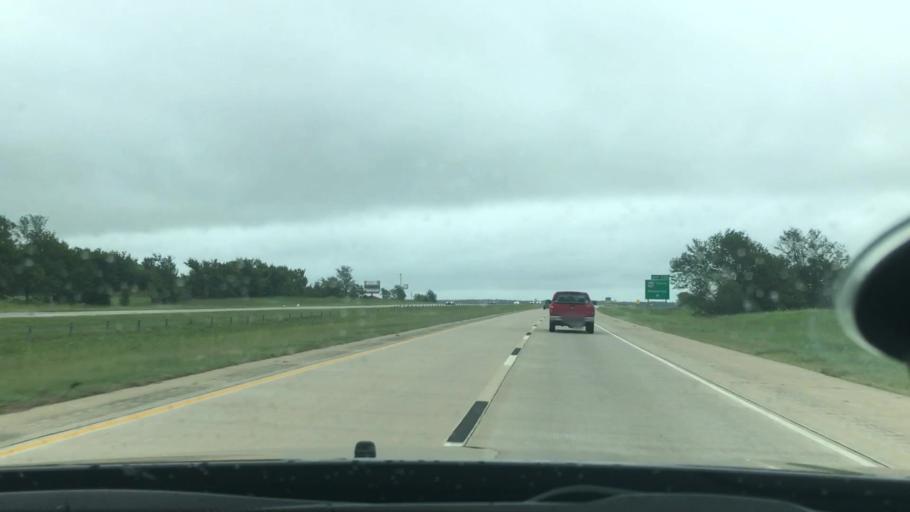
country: US
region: Oklahoma
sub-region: Okmulgee County
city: Wilson
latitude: 35.4312
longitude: -96.1308
